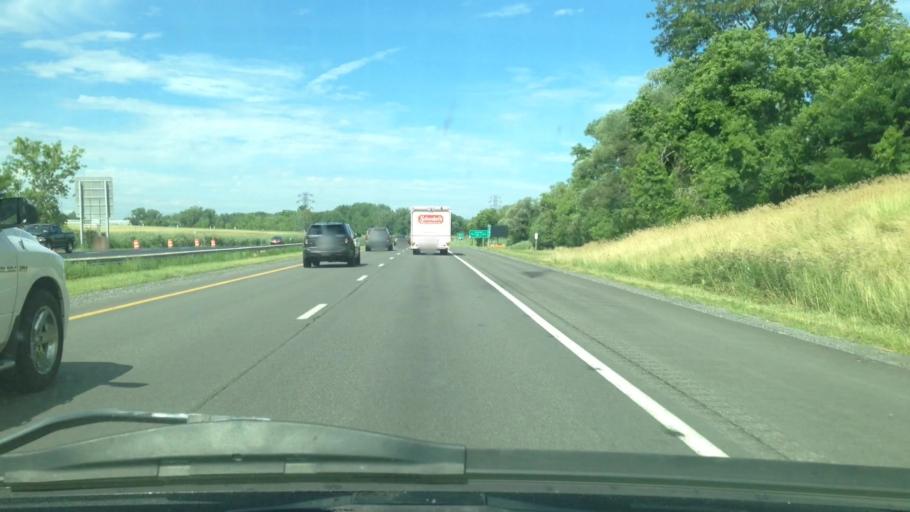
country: US
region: New York
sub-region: Onondaga County
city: Mattydale
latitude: 43.0922
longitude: -76.1491
